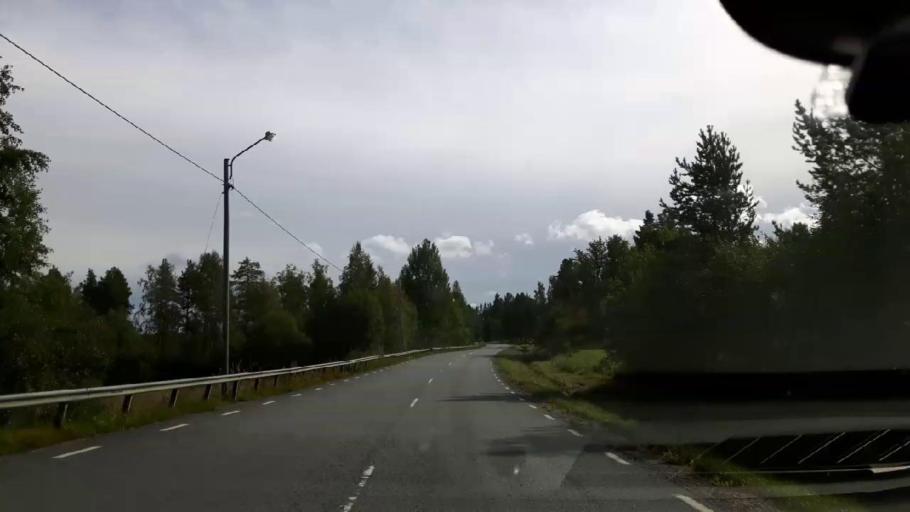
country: SE
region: Jaemtland
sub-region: Braecke Kommun
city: Braecke
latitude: 63.1521
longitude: 15.7247
